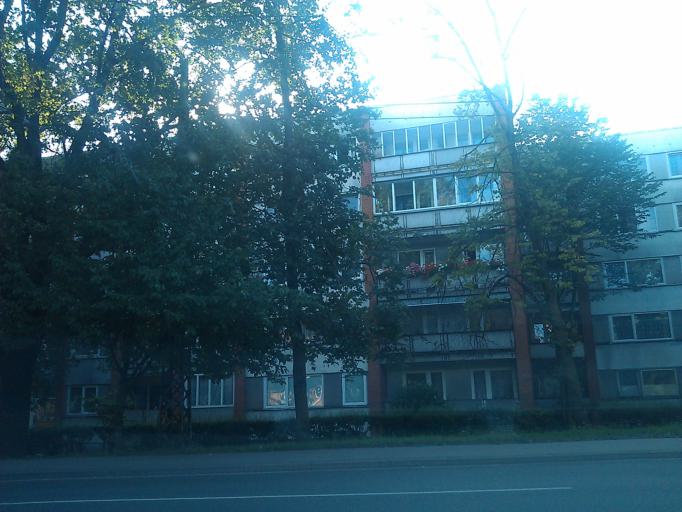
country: LV
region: Riga
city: Jaunciems
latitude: 56.9670
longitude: 24.1770
